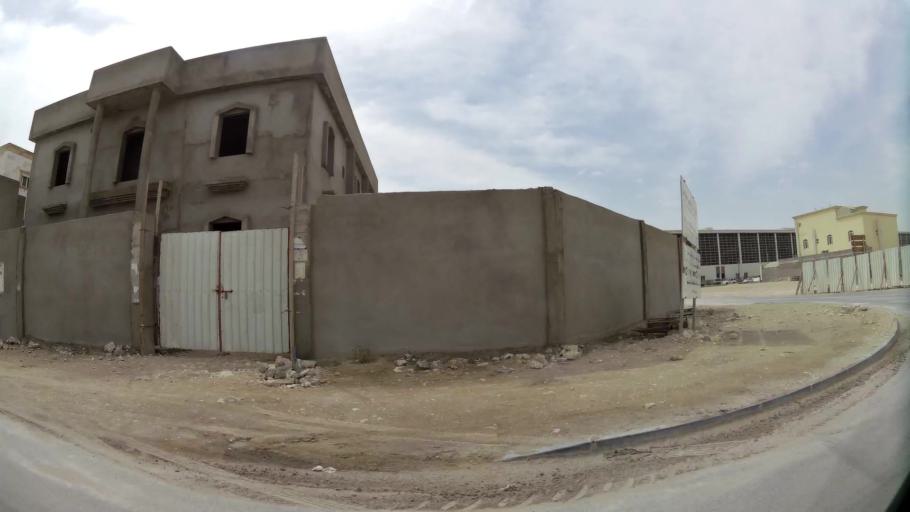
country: QA
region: Al Wakrah
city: Al Wukayr
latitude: 25.1966
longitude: 51.4583
